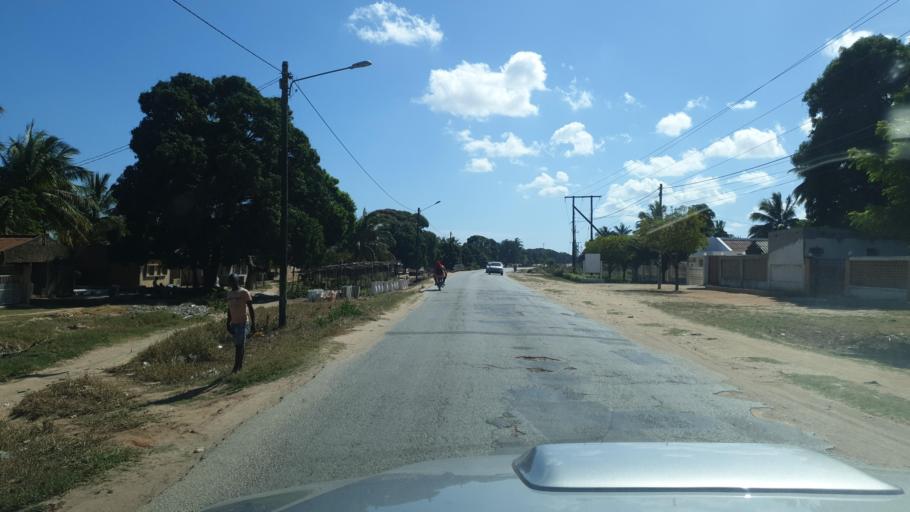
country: MZ
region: Nampula
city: Nacala
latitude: -14.5199
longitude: 40.6956
